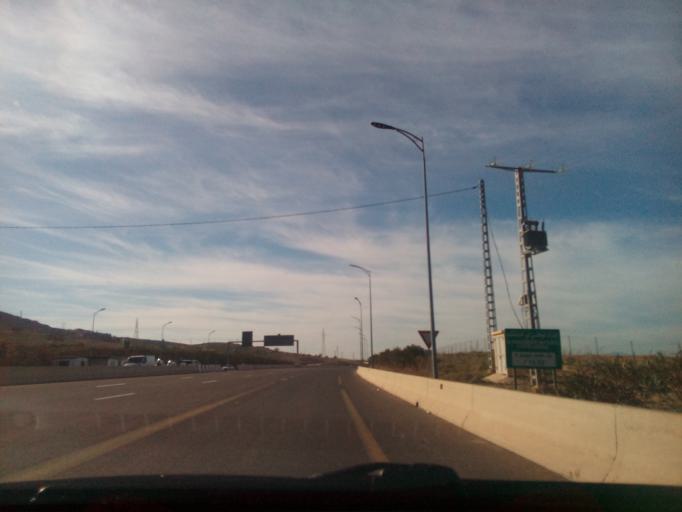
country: DZ
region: Tlemcen
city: Hennaya
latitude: 34.9189
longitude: -1.3716
